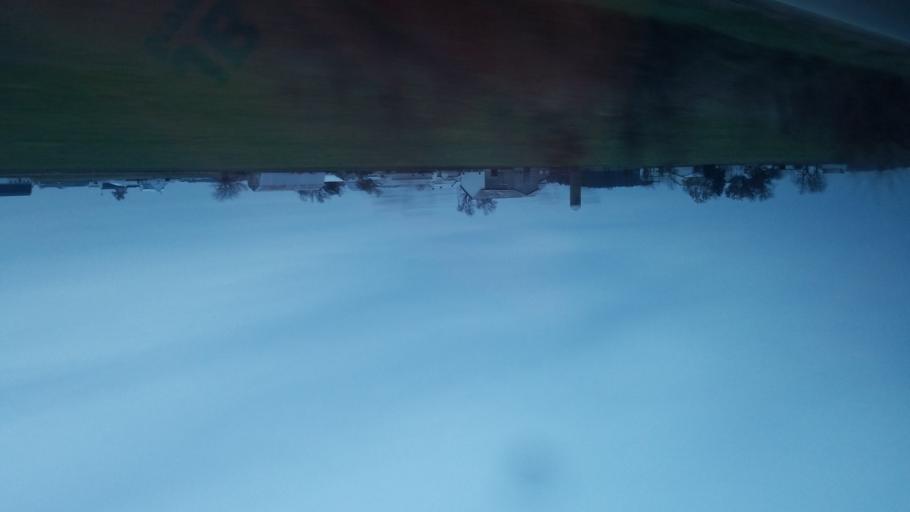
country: US
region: Indiana
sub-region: Adams County
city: Berne
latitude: 40.7166
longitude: -84.9010
